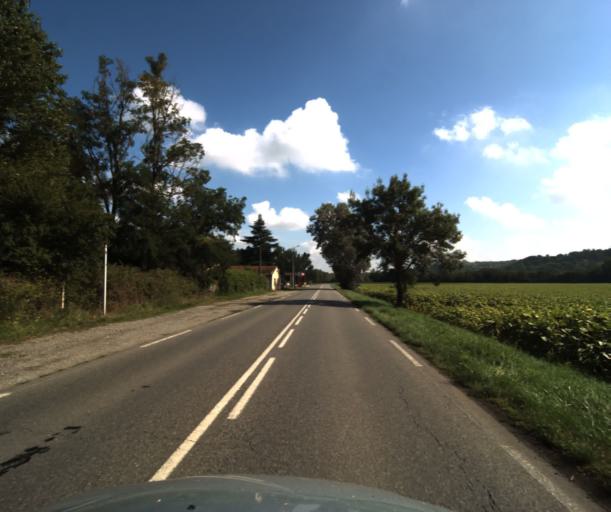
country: FR
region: Midi-Pyrenees
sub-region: Departement de la Haute-Garonne
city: Portet-sur-Garonne
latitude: 43.5168
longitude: 1.4176
